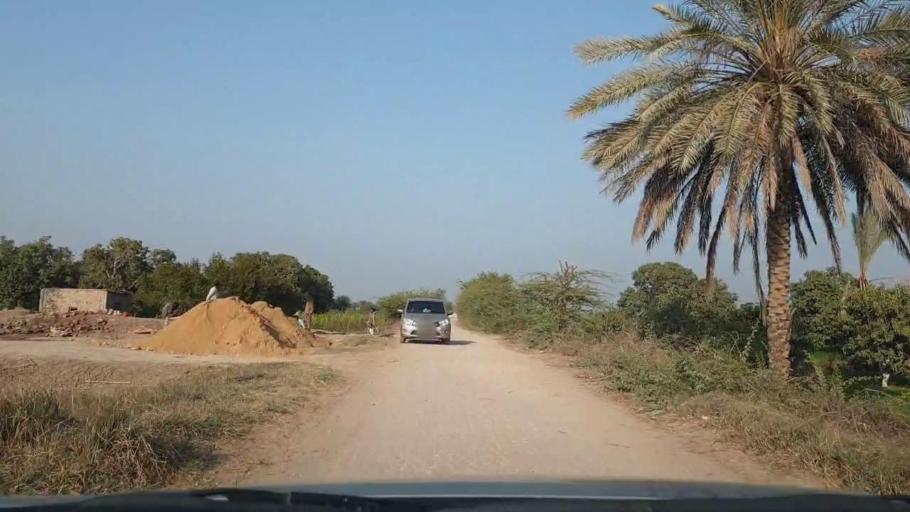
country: PK
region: Sindh
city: Tando Adam
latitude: 25.6665
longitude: 68.6345
